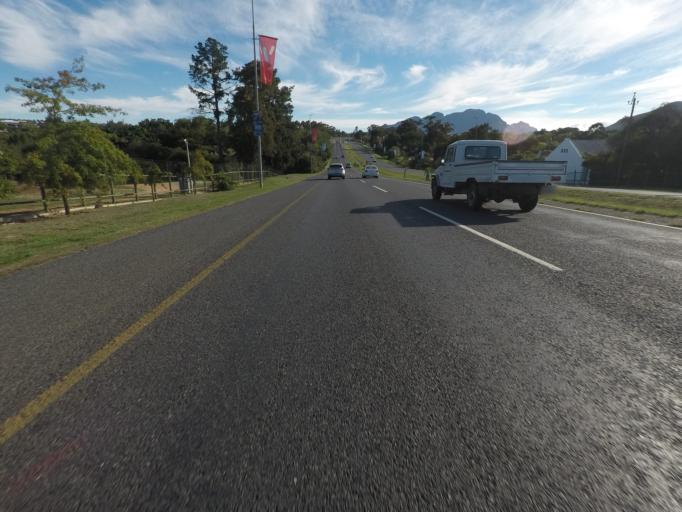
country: ZA
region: Western Cape
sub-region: Cape Winelands District Municipality
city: Stellenbosch
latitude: -33.9735
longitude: 18.8424
